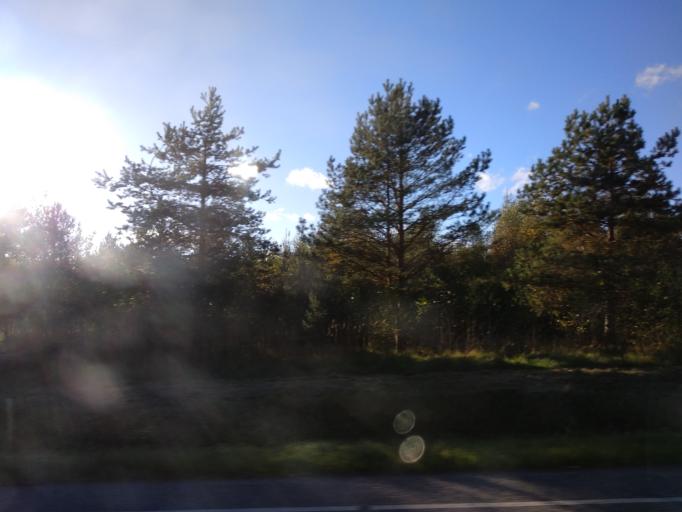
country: EE
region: Polvamaa
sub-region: Polva linn
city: Polva
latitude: 58.0304
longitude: 27.0659
